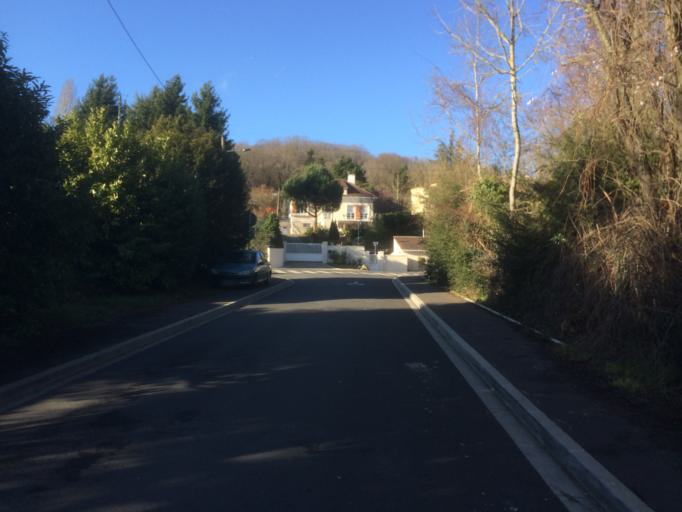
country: FR
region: Ile-de-France
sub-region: Departement de l'Essonne
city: Igny
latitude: 48.7357
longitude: 2.2174
